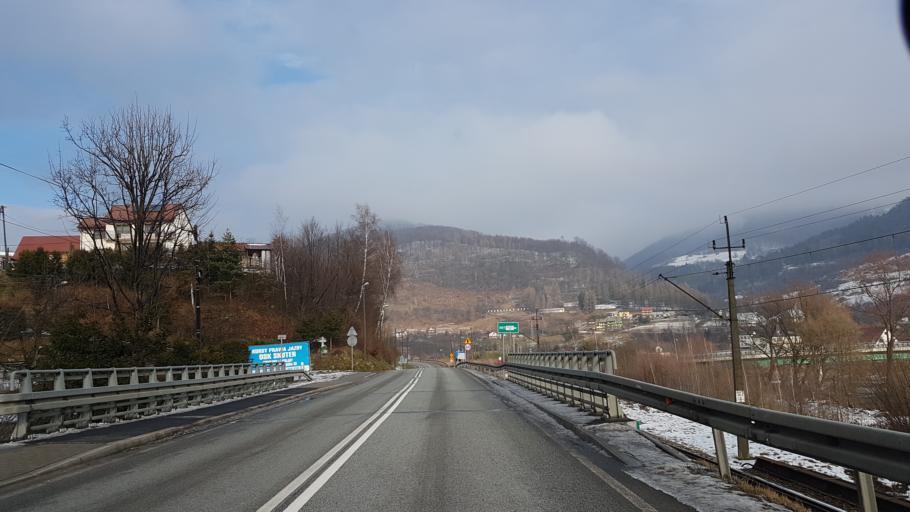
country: PL
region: Lesser Poland Voivodeship
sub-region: Powiat nowosadecki
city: Piwniczna-Zdroj
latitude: 49.4640
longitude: 20.6967
